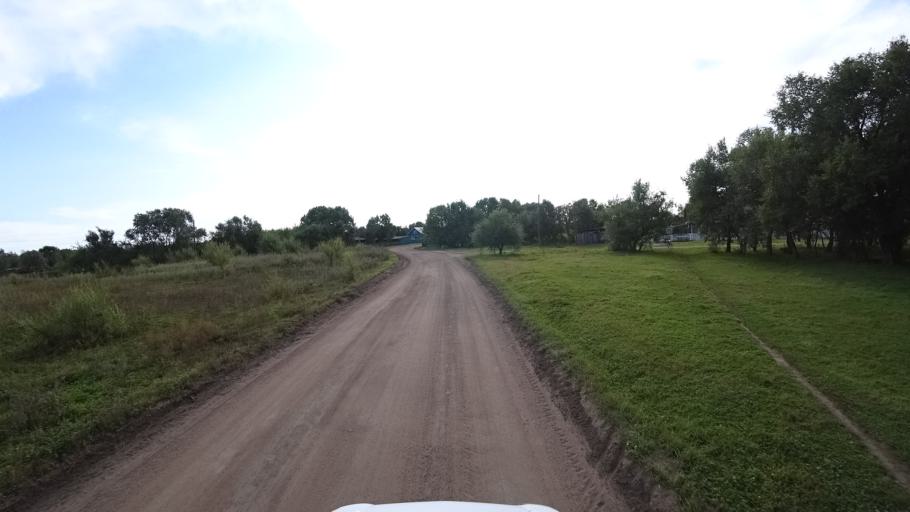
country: RU
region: Amur
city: Arkhara
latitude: 49.3532
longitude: 130.1082
